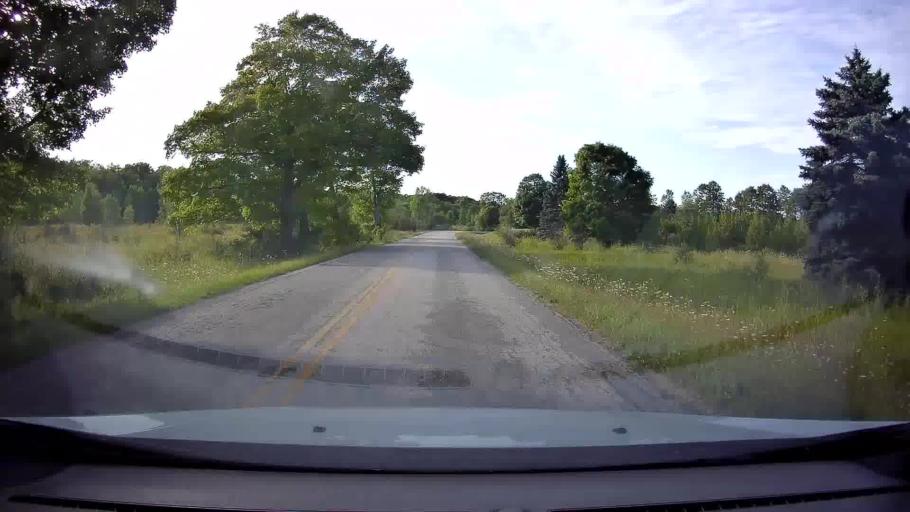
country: US
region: Wisconsin
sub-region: Door County
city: Sturgeon Bay
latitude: 45.1762
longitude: -87.1419
